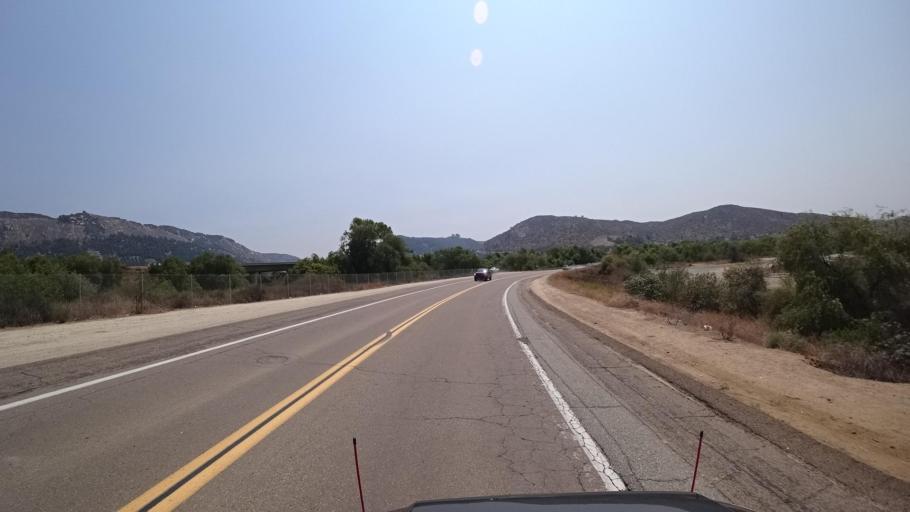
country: US
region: California
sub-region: San Diego County
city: Bonsall
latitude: 33.3255
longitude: -117.1605
